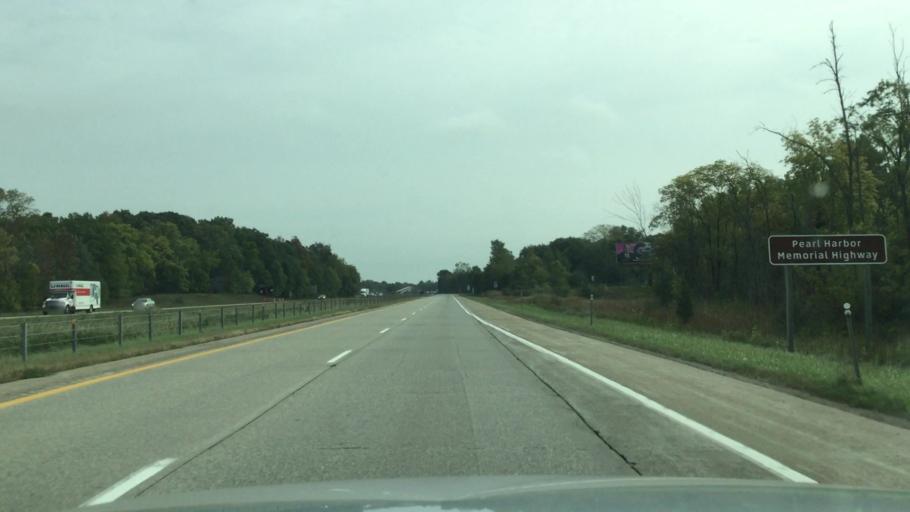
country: US
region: Michigan
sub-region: Shiawassee County
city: Perry
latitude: 42.8405
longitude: -84.2102
